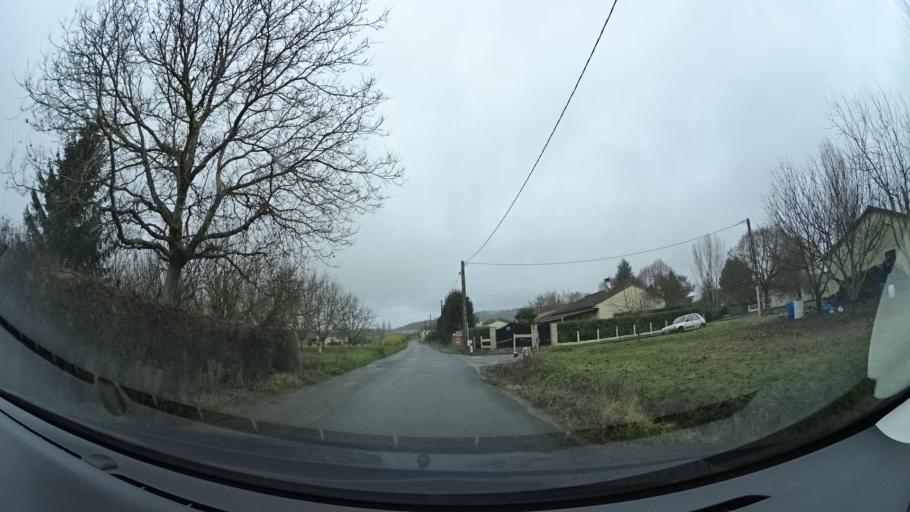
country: FR
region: Midi-Pyrenees
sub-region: Departement du Lot
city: Prayssac
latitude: 44.4849
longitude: 1.1984
